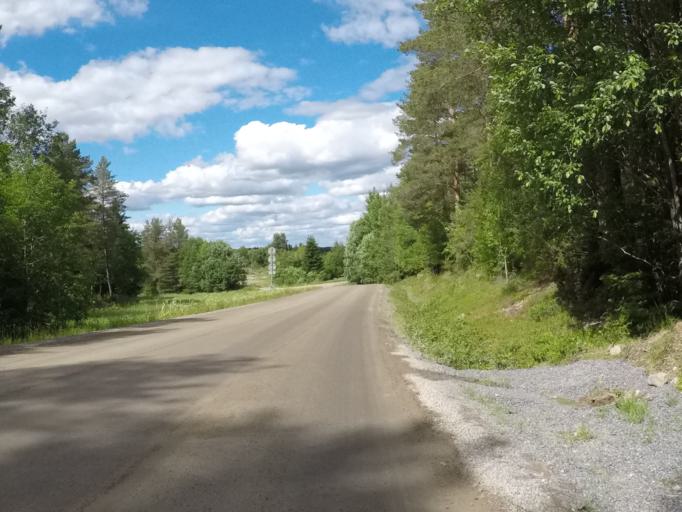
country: SE
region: Vaesterbotten
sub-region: Robertsfors Kommun
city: Robertsfors
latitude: 64.1380
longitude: 20.9005
